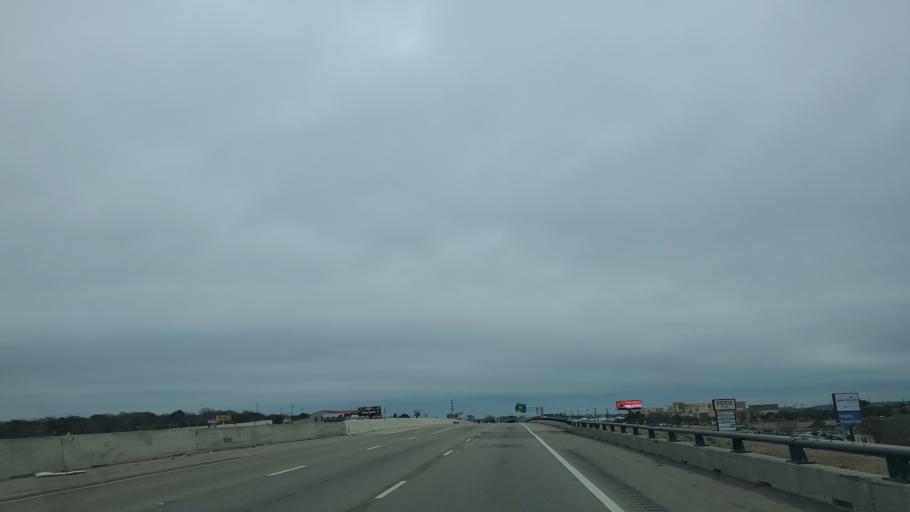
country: US
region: Texas
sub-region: Bell County
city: Harker Heights
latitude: 31.0763
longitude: -97.6894
